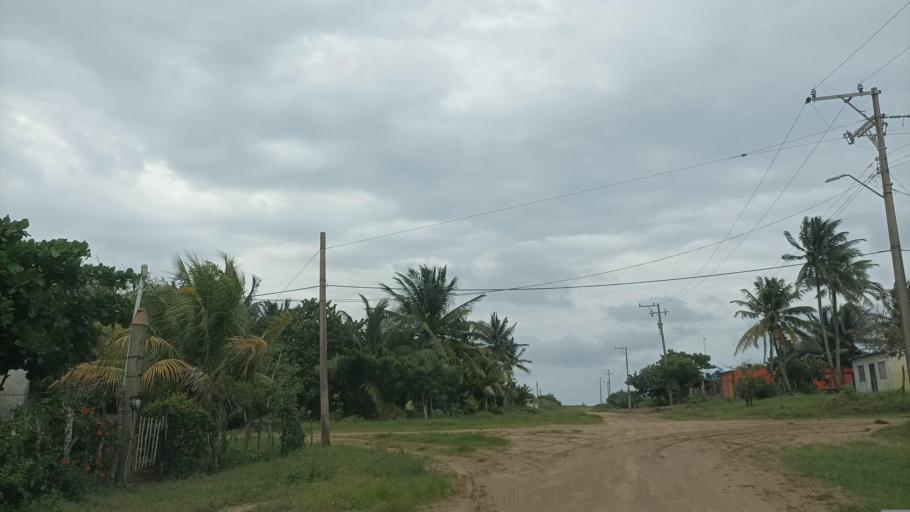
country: MX
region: Veracruz
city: Agua Dulce
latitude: 18.2082
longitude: -94.1408
